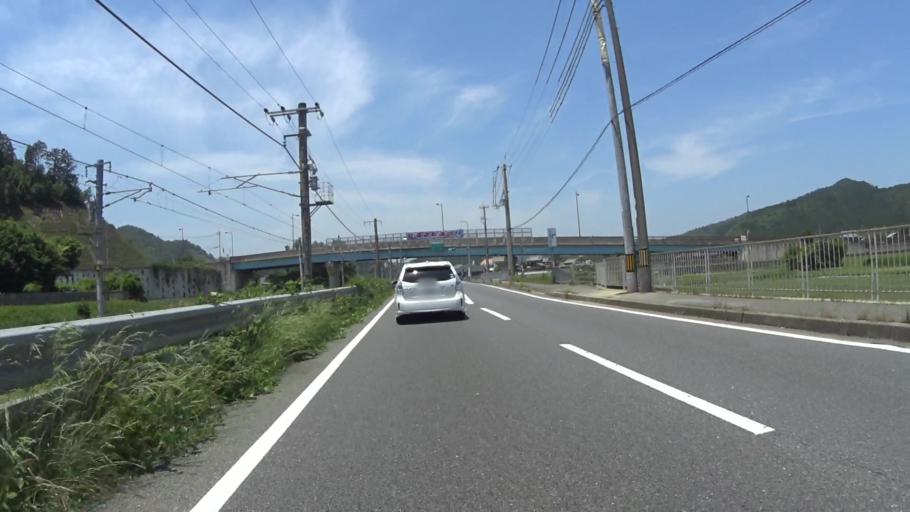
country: JP
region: Kyoto
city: Kameoka
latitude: 35.0734
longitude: 135.5259
